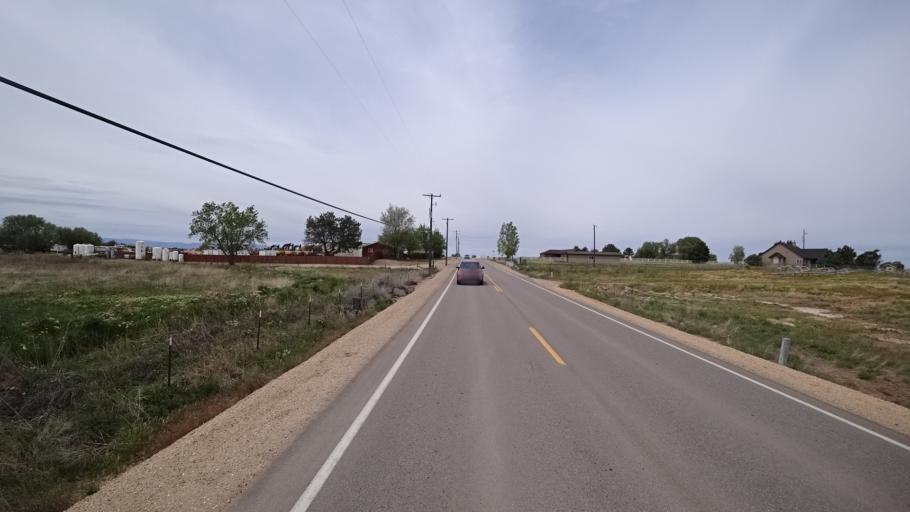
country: US
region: Idaho
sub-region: Ada County
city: Kuna
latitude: 43.5319
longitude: -116.3637
